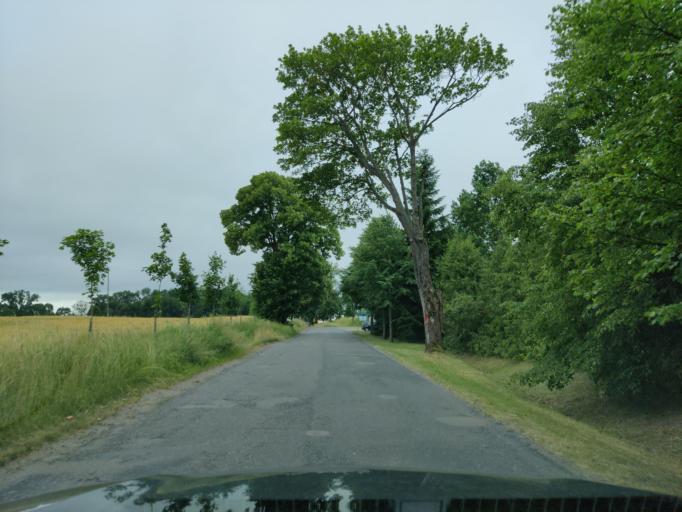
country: PL
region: Warmian-Masurian Voivodeship
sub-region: Powiat gizycki
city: Ryn
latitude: 53.9290
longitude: 21.5505
